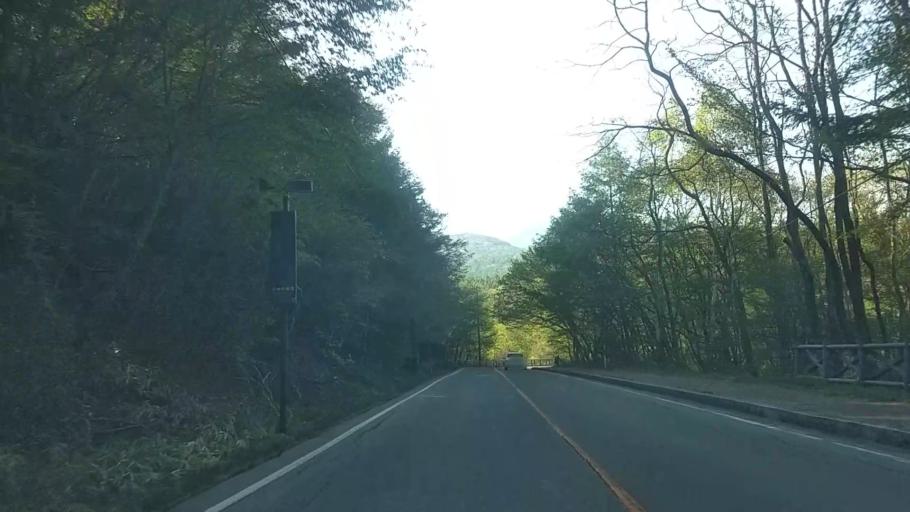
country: JP
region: Yamanashi
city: Nirasaki
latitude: 35.9208
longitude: 138.4058
